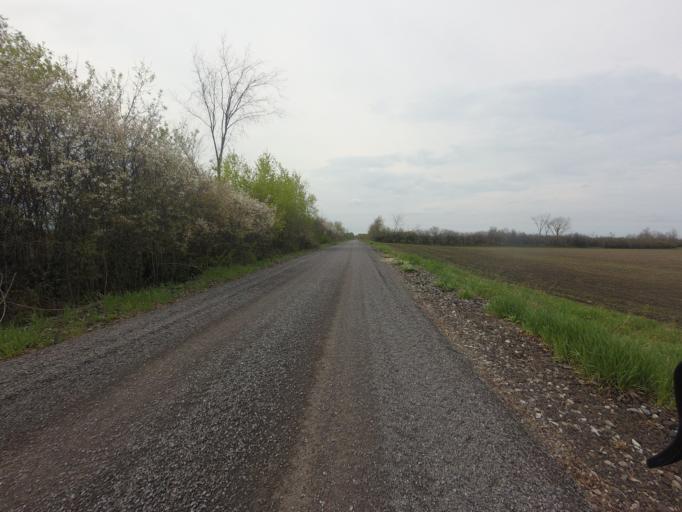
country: CA
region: Ontario
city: Carleton Place
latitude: 45.1932
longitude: -76.1634
